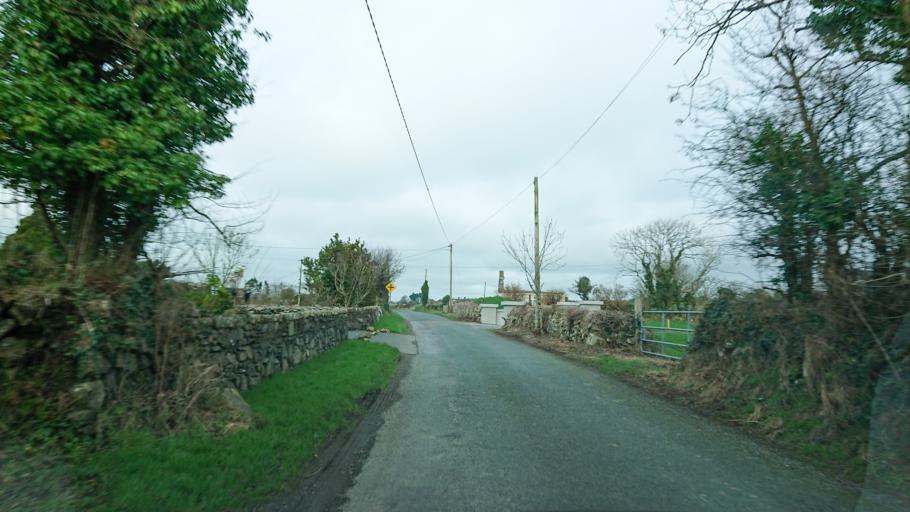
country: IE
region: Munster
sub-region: Waterford
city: Portlaw
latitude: 52.1630
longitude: -7.3058
